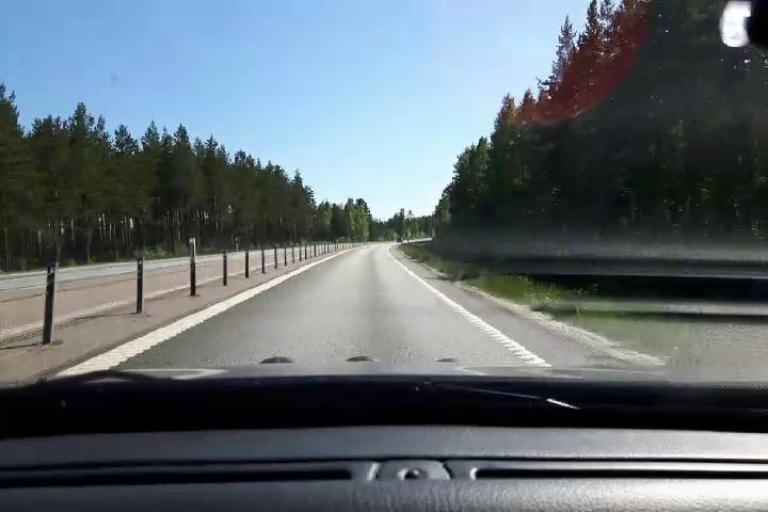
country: SE
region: Gaevleborg
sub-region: Soderhamns Kommun
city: Ljusne
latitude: 61.1149
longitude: 17.0127
